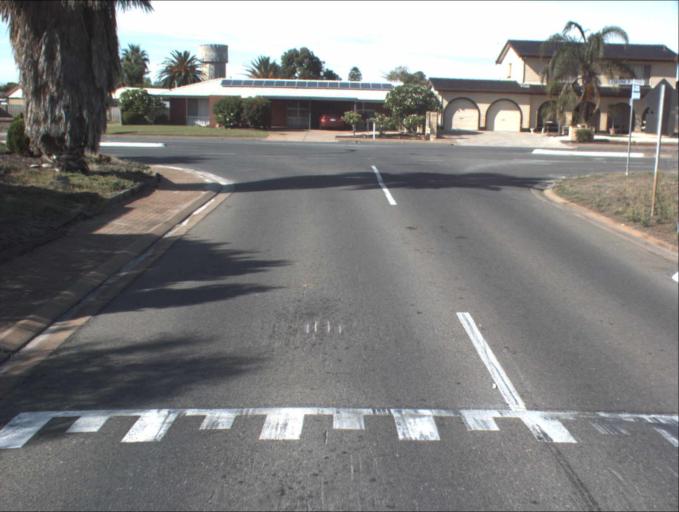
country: AU
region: South Australia
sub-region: Port Adelaide Enfield
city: Birkenhead
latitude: -34.7921
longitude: 138.4954
